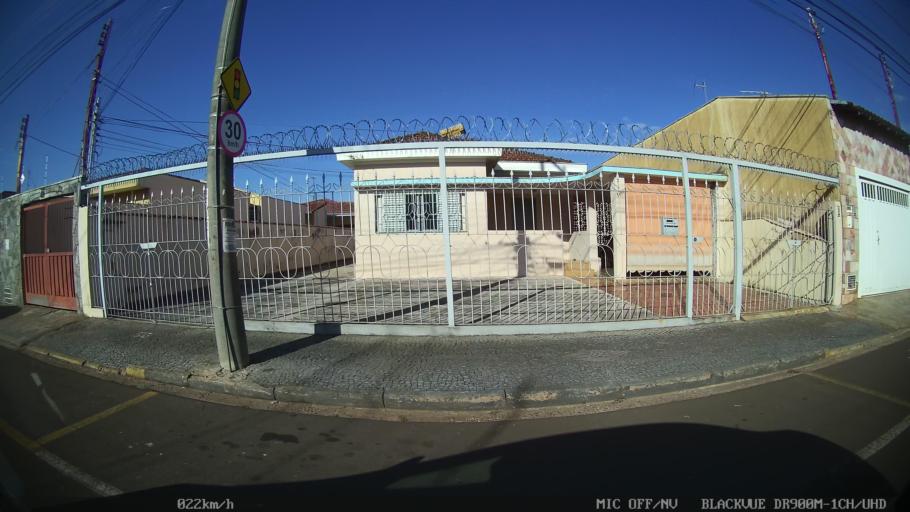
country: BR
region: Sao Paulo
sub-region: Franca
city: Franca
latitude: -20.5320
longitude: -47.4162
